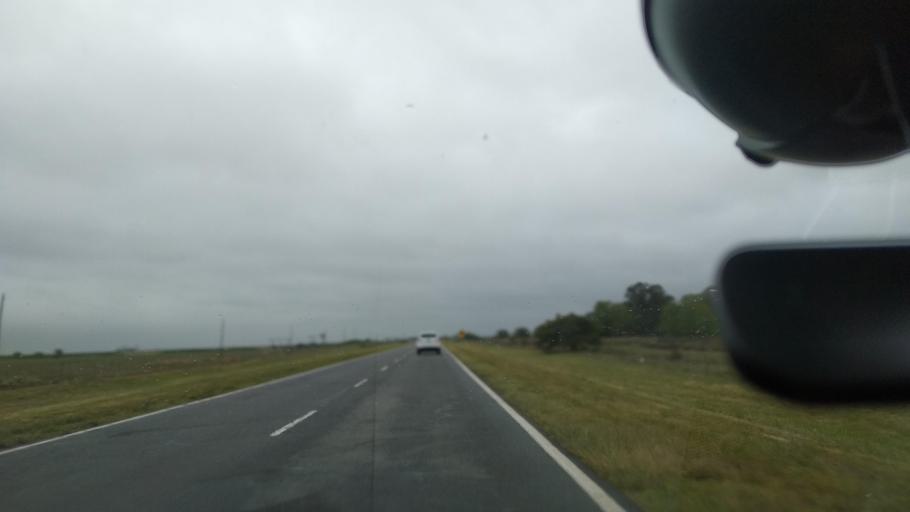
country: AR
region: Buenos Aires
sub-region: Partido de Dolores
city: Dolores
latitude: -36.0997
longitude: -57.4337
